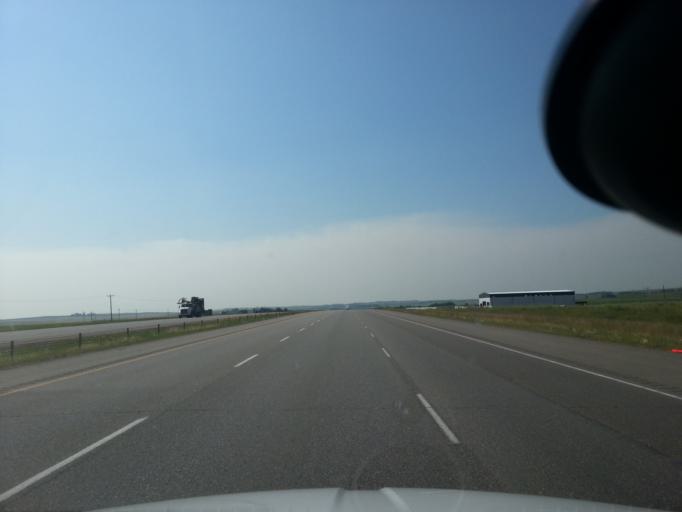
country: CA
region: Alberta
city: Crossfield
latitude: 51.4964
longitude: -114.0253
